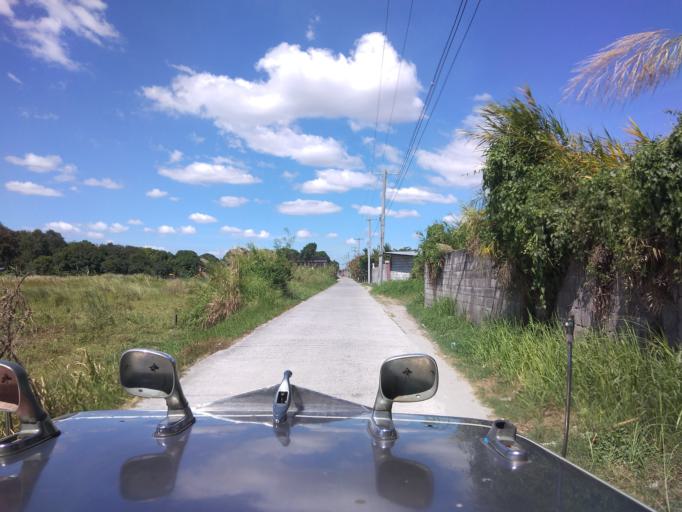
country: PH
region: Central Luzon
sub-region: Province of Pampanga
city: Magliman
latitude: 15.0521
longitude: 120.6411
